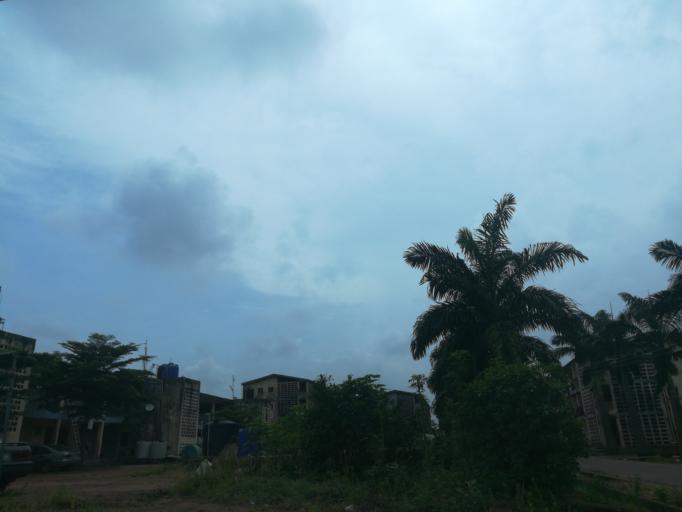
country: NG
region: Lagos
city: Oshodi
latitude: 6.5698
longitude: 3.3540
